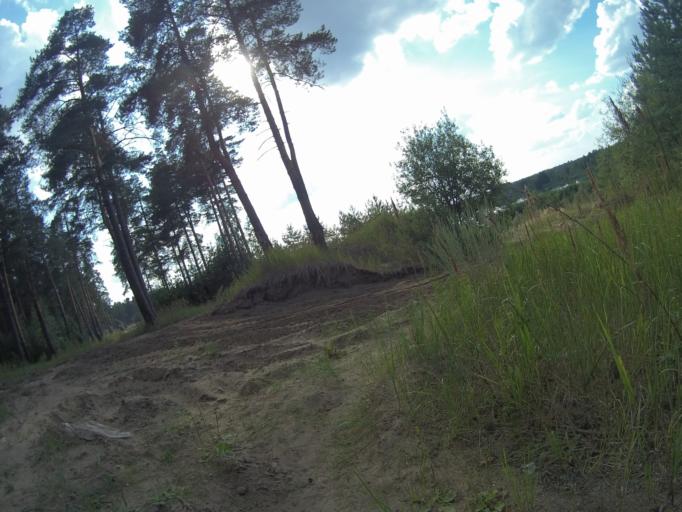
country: RU
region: Vladimir
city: Kommunar
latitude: 56.0389
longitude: 40.4260
